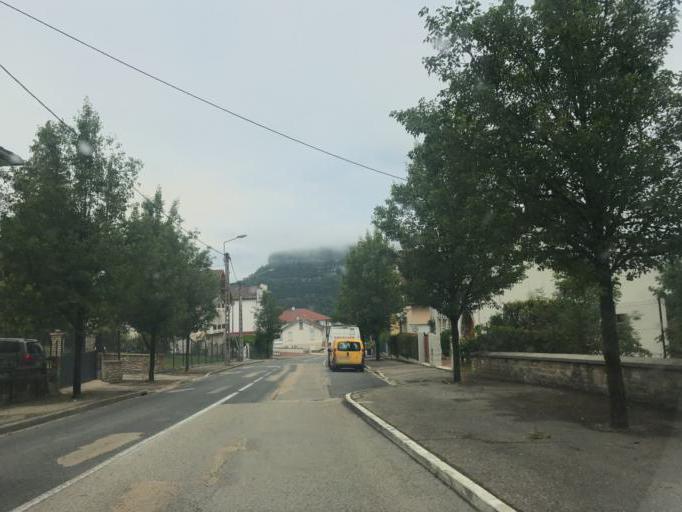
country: FR
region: Rhone-Alpes
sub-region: Departement de l'Ain
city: Dortan
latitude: 46.3148
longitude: 5.6589
